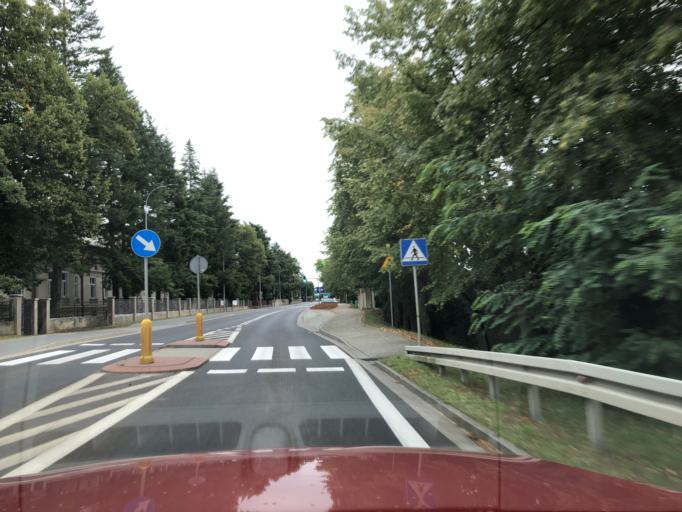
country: PL
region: Greater Poland Voivodeship
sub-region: Powiat szamotulski
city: Pniewy
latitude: 52.5167
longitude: 16.2446
